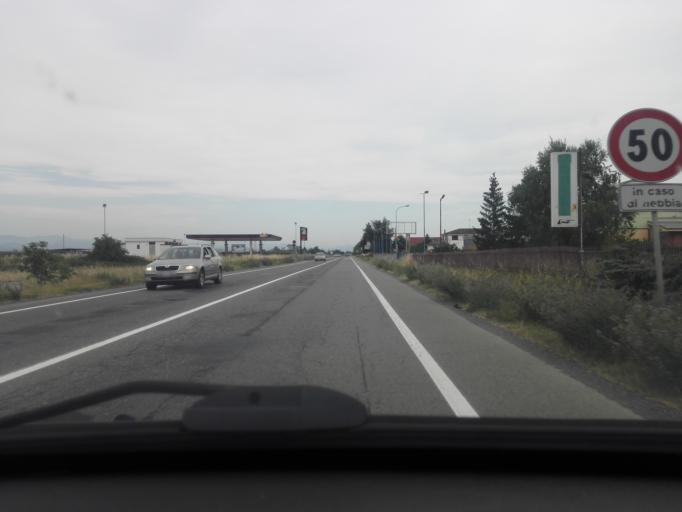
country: IT
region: Piedmont
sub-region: Provincia di Alessandria
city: Mandrogne
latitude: 44.8355
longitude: 8.7359
